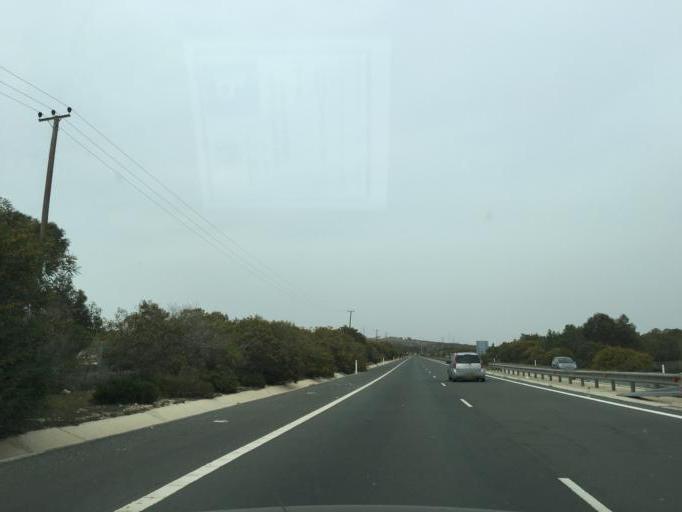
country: CY
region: Ammochostos
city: Ayia Napa
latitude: 34.9965
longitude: 33.9709
